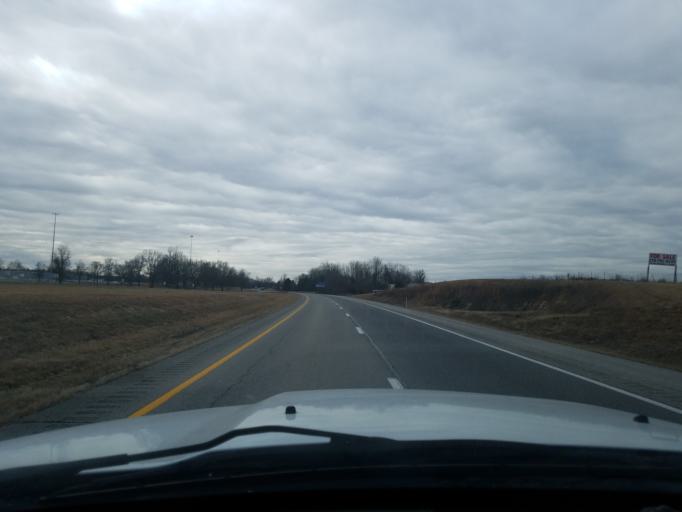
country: US
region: Kentucky
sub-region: Ohio County
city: Beaver Dam
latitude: 37.3772
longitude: -86.8275
